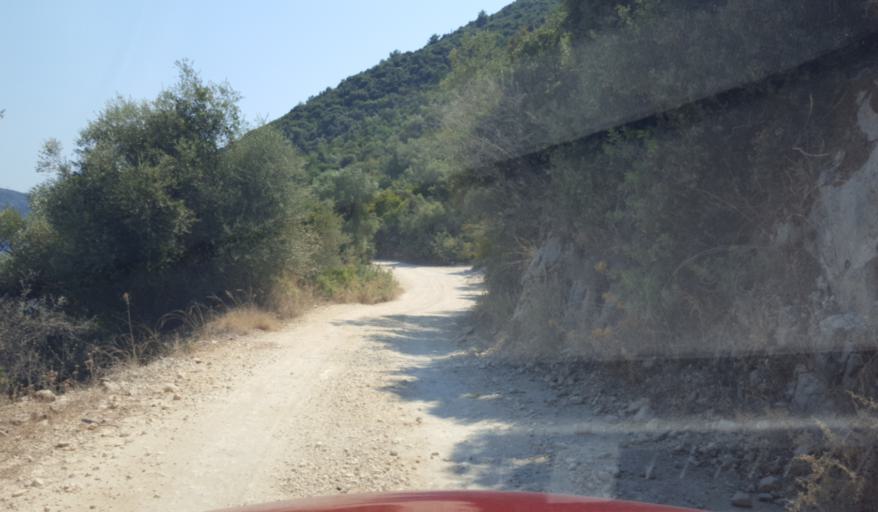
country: GR
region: Ionian Islands
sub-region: Lefkada
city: Nidri
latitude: 38.6653
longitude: 20.7126
